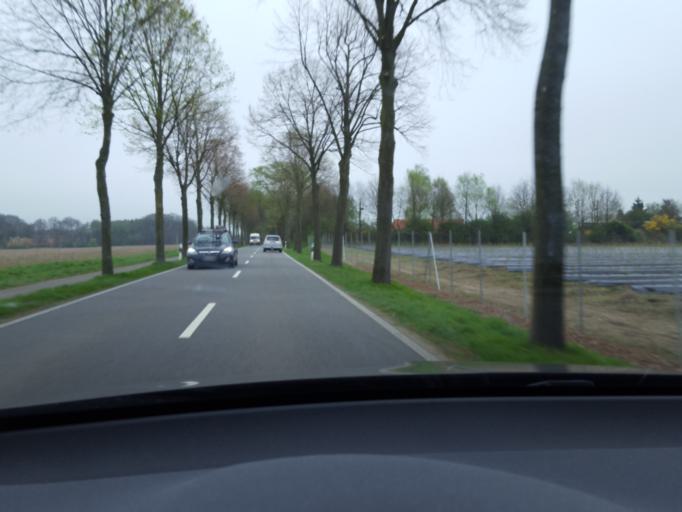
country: DE
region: North Rhine-Westphalia
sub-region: Regierungsbezirk Munster
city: Raesfeld
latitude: 51.7498
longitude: 6.8753
